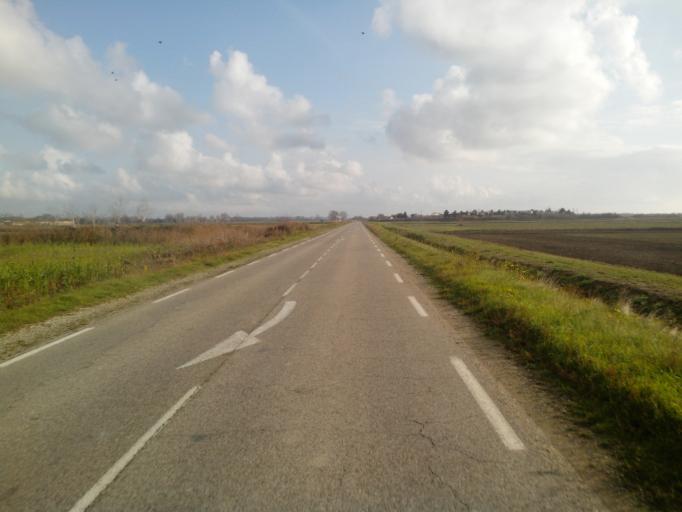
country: FR
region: Provence-Alpes-Cote d'Azur
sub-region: Departement des Bouches-du-Rhone
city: Port-Saint-Louis-du-Rhone
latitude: 43.4685
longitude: 4.7088
